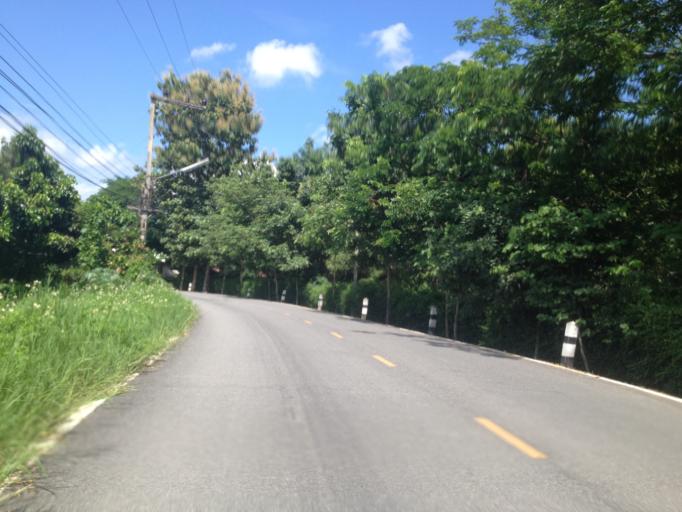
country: TH
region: Chiang Mai
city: Hang Dong
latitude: 18.6653
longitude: 98.9681
